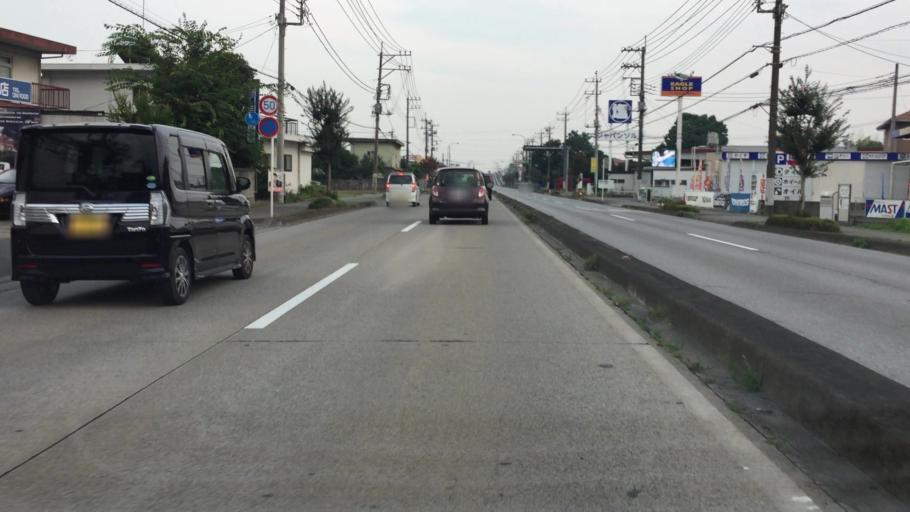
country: JP
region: Tochigi
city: Tochigi
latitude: 36.3703
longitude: 139.7155
